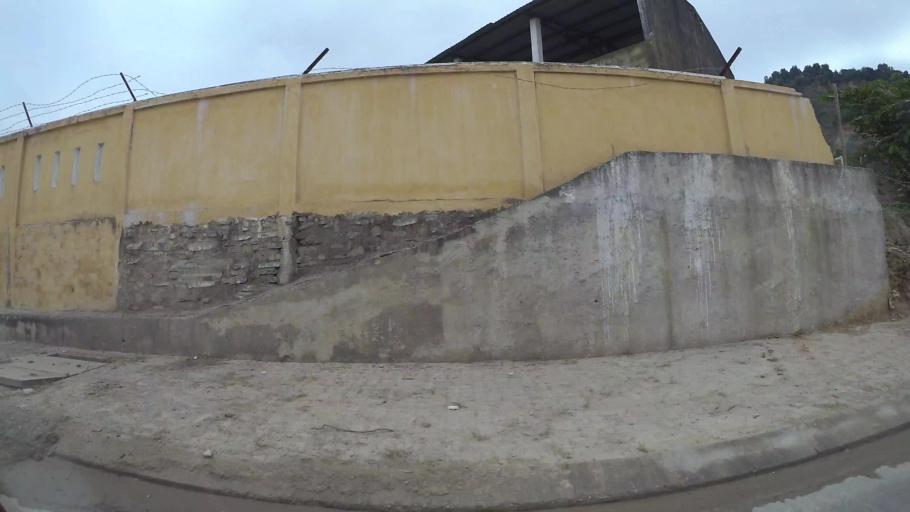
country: VN
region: Da Nang
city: Lien Chieu
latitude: 16.0429
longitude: 108.1637
